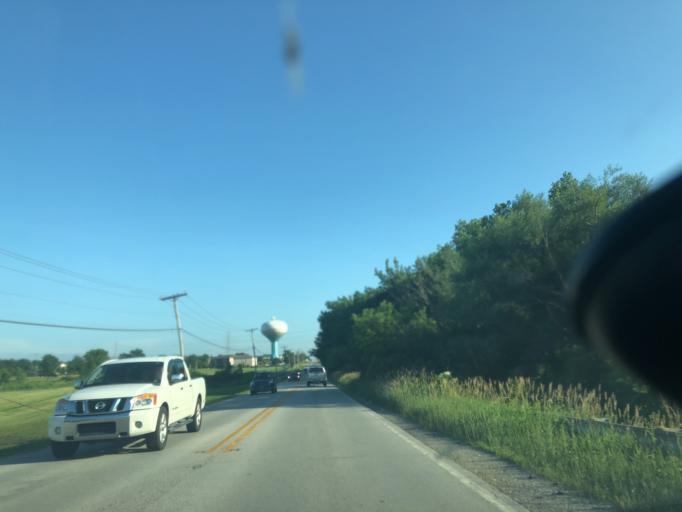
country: US
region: Illinois
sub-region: Will County
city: Mokena
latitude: 41.5718
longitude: -87.8906
